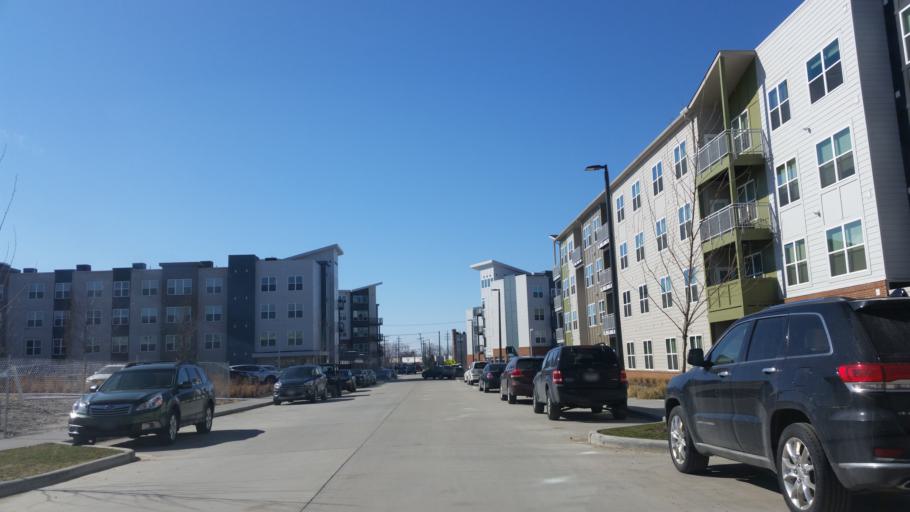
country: US
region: Ohio
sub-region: Cuyahoga County
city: Cleveland
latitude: 41.4894
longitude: -81.7271
